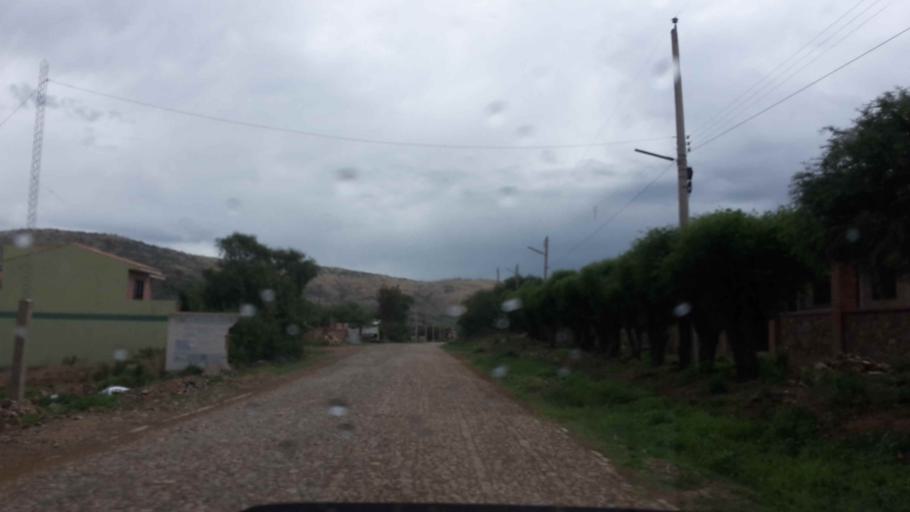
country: BO
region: Cochabamba
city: Tarata
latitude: -17.5494
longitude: -66.1665
